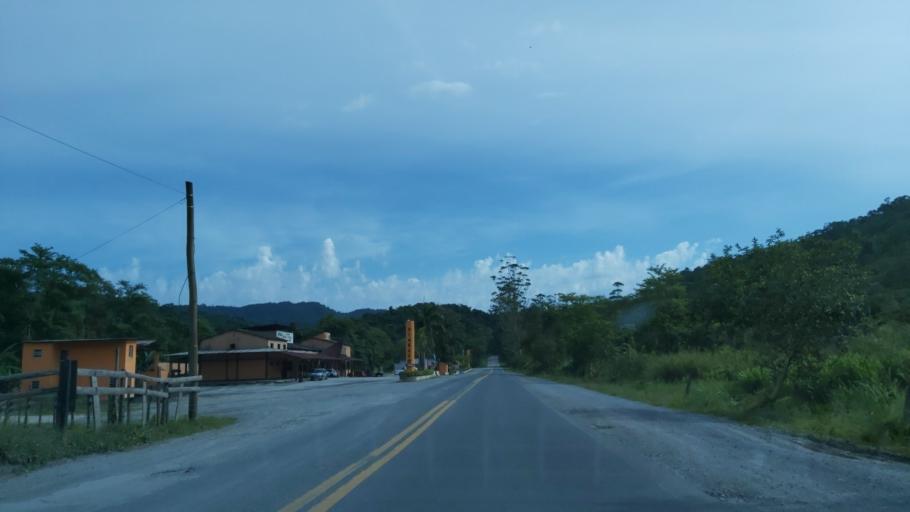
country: BR
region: Sao Paulo
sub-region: Miracatu
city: Miracatu
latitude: -24.0623
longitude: -47.5902
